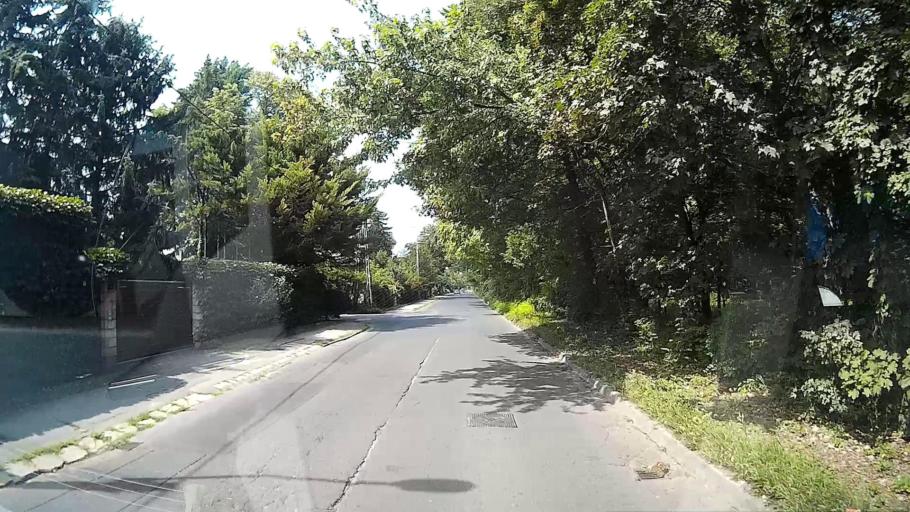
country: HU
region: Budapest
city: Budapest III. keruelet
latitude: 47.5729
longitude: 19.0544
